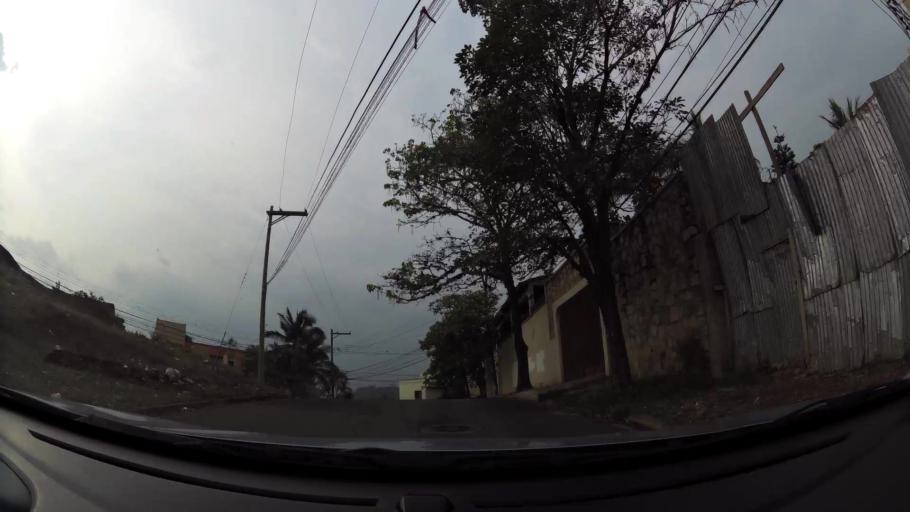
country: HN
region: Francisco Morazan
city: Tegucigalpa
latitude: 14.0813
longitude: -87.1972
